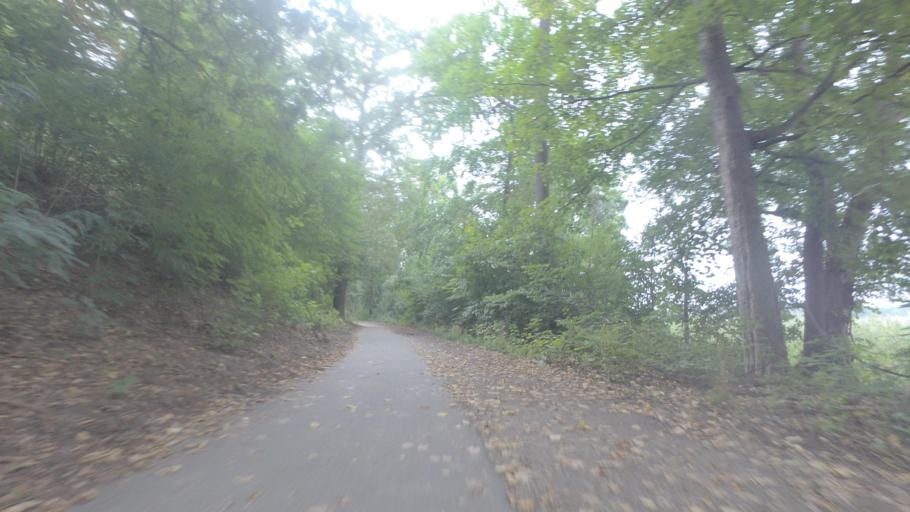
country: DE
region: Berlin
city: Kladow
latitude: 52.4277
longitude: 13.1206
